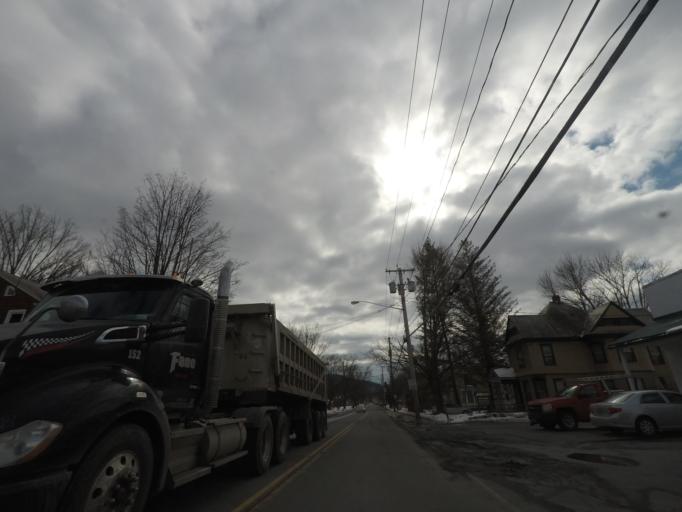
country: US
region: New York
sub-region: Washington County
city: Cambridge
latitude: 43.0271
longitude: -73.3761
